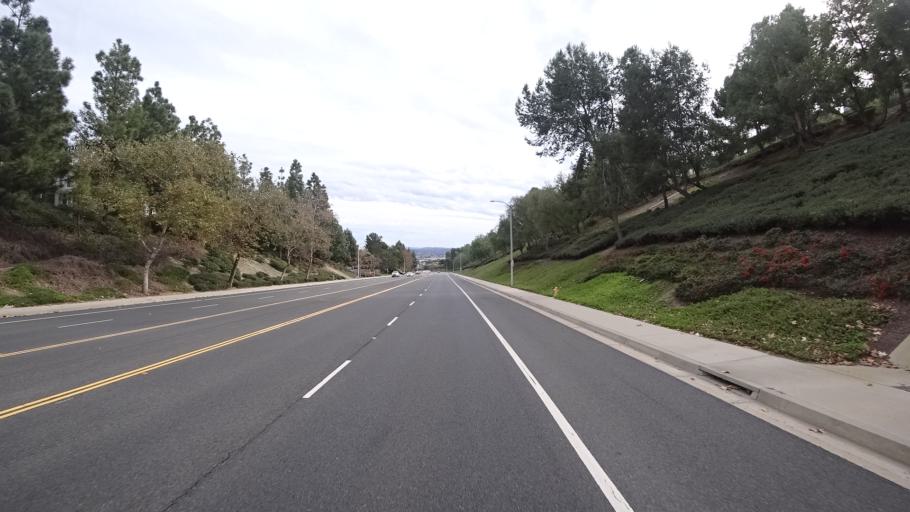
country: US
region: California
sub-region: Orange County
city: Aliso Viejo
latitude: 33.5753
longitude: -117.7391
